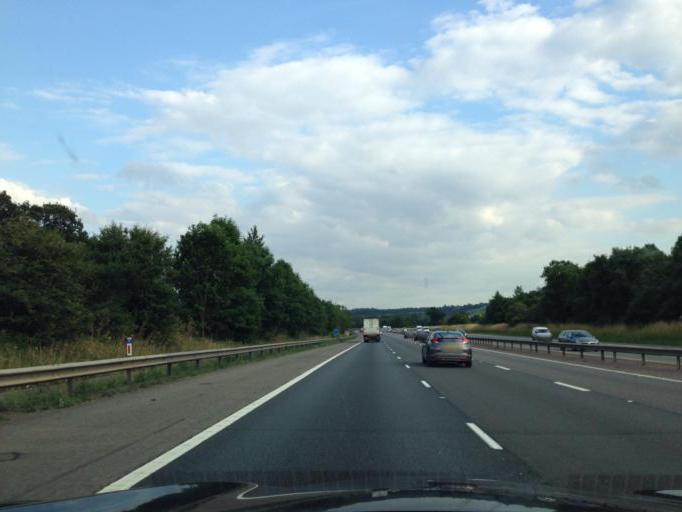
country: GB
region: England
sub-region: Oxfordshire
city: Hanwell
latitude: 52.1467
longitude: -1.4162
